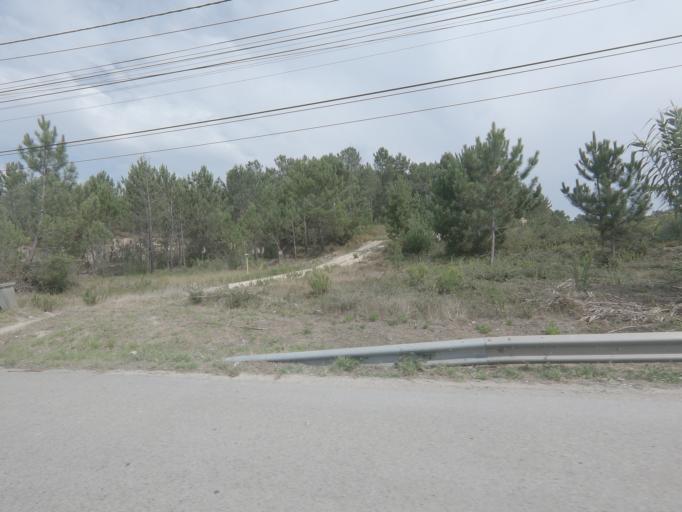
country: PT
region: Leiria
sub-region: Leiria
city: Caranguejeira
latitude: 39.8303
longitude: -8.7209
